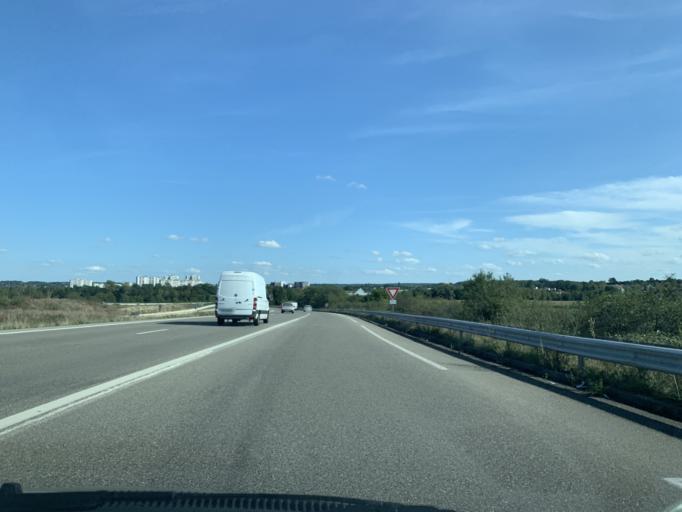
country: FR
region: Alsace
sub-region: Departement du Haut-Rhin
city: Lutterbach
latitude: 47.7459
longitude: 7.2771
